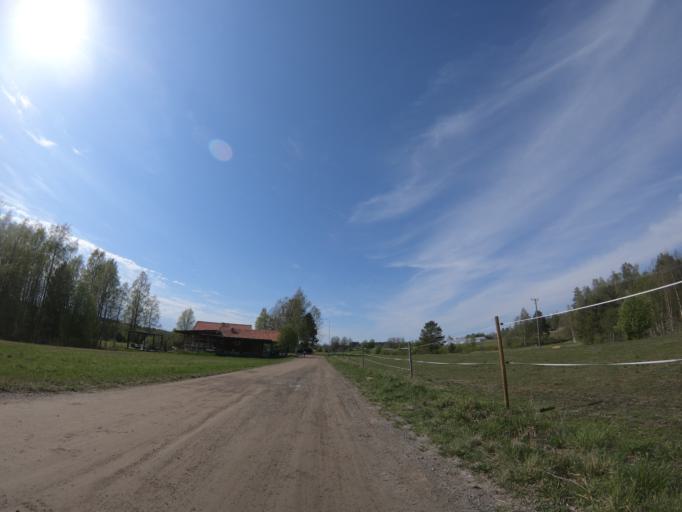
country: SE
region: Vaesterbotten
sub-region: Umea Kommun
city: Roback
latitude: 63.8290
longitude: 20.1935
